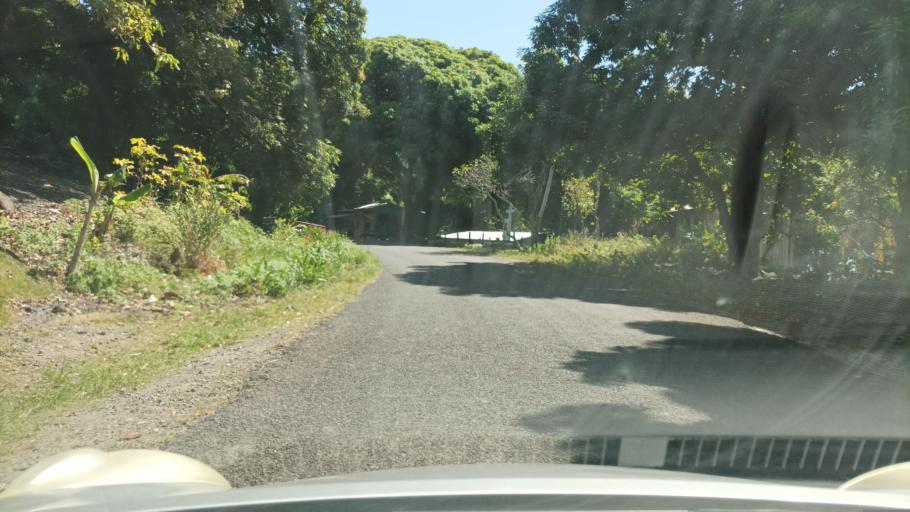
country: SB
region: Guadalcanal
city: Honiara
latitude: -9.2529
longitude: 159.7133
